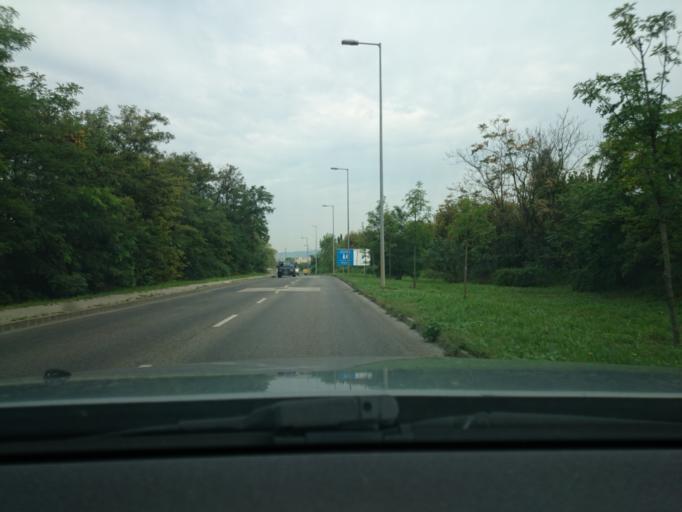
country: HU
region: Budapest
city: Budapest XX. keruelet
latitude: 47.4603
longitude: 19.0926
